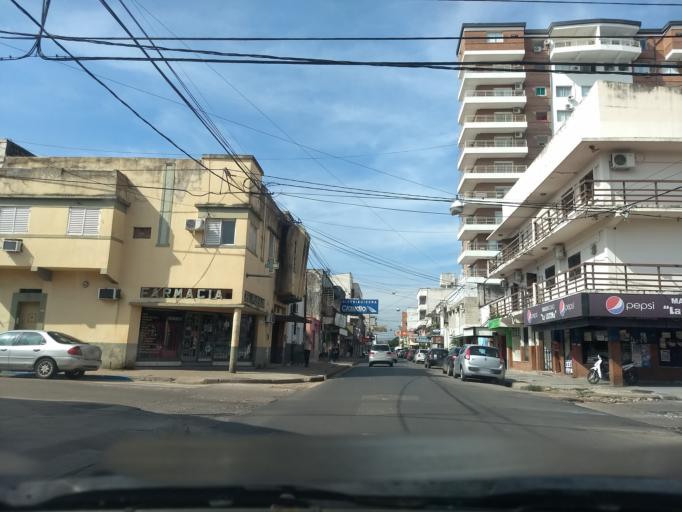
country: AR
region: Corrientes
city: Corrientes
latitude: -27.4697
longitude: -58.8256
